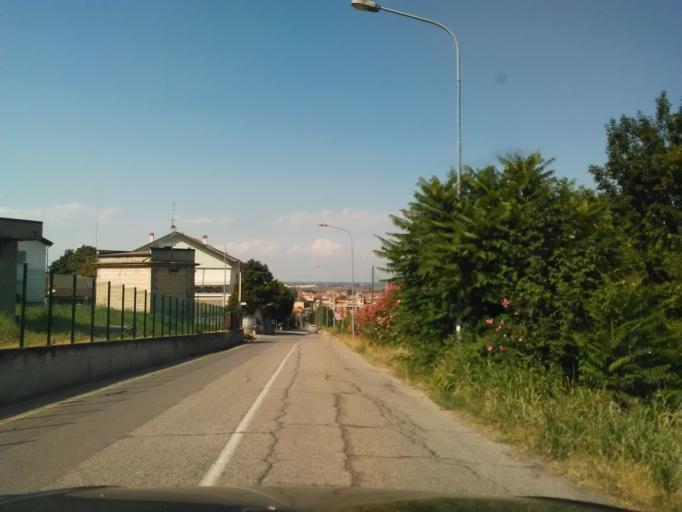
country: IT
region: Piedmont
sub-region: Provincia di Alessandria
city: Casale Monferrato
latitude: 45.1270
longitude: 8.4406
